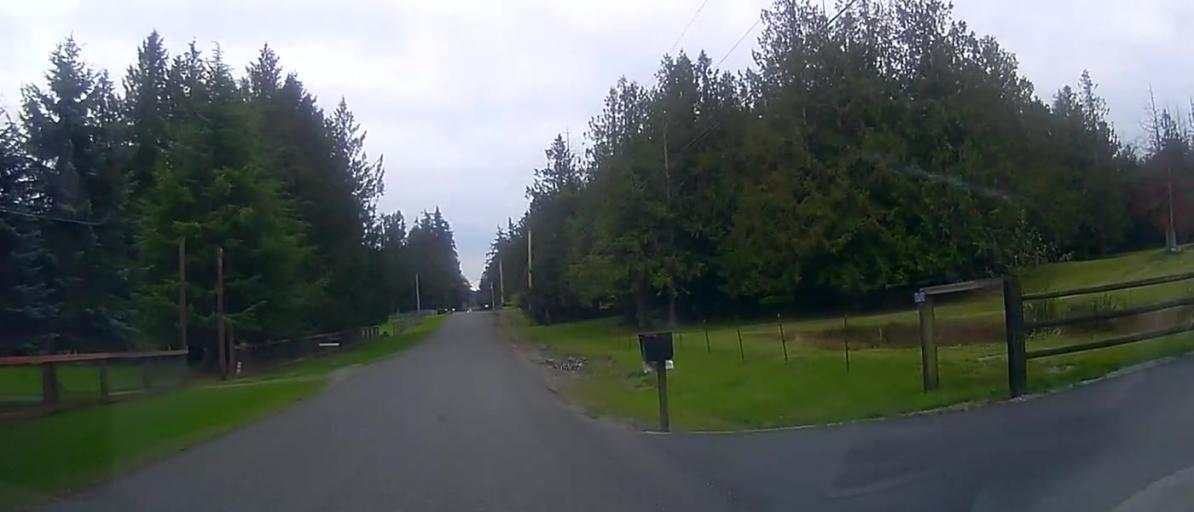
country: US
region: Washington
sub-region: Skagit County
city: Burlington
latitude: 48.4472
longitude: -122.2945
